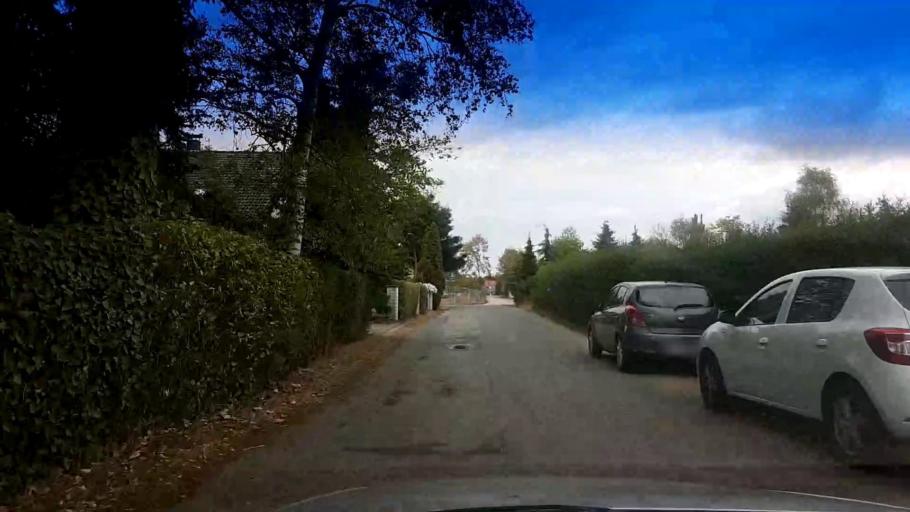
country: DE
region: Bavaria
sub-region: Upper Franconia
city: Bamberg
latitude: 49.8773
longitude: 10.9238
